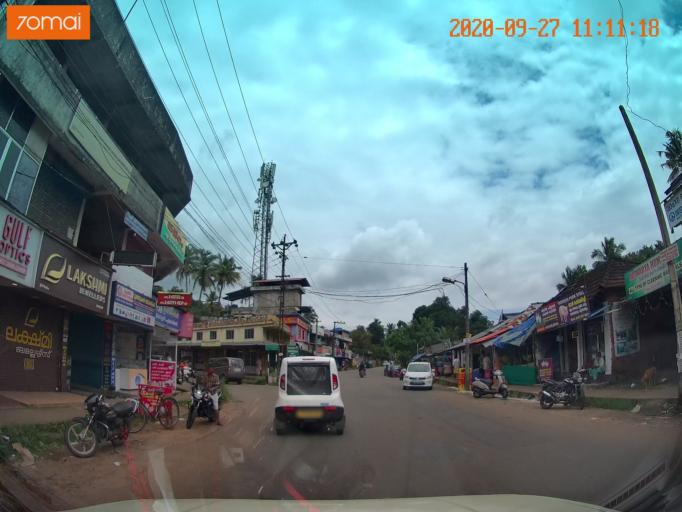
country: IN
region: Kerala
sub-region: Thrissur District
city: Thanniyam
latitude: 10.4317
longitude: 76.2167
